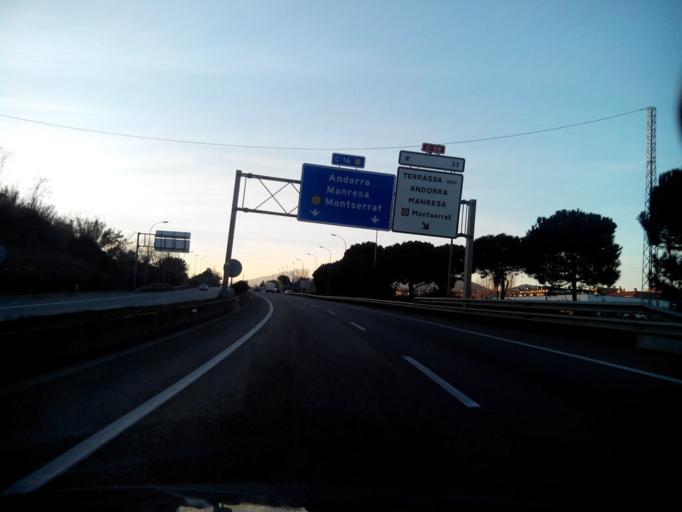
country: ES
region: Catalonia
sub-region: Provincia de Barcelona
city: Terrassa
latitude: 41.5549
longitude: 1.9964
